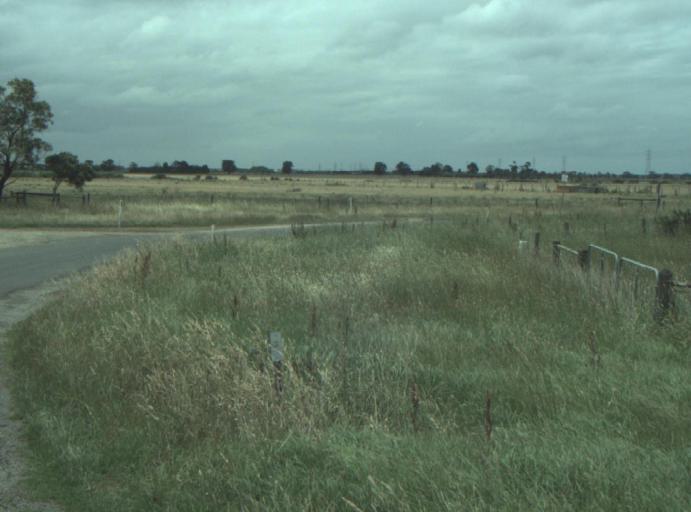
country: AU
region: Victoria
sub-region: Greater Geelong
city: Breakwater
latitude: -38.2221
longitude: 144.3754
